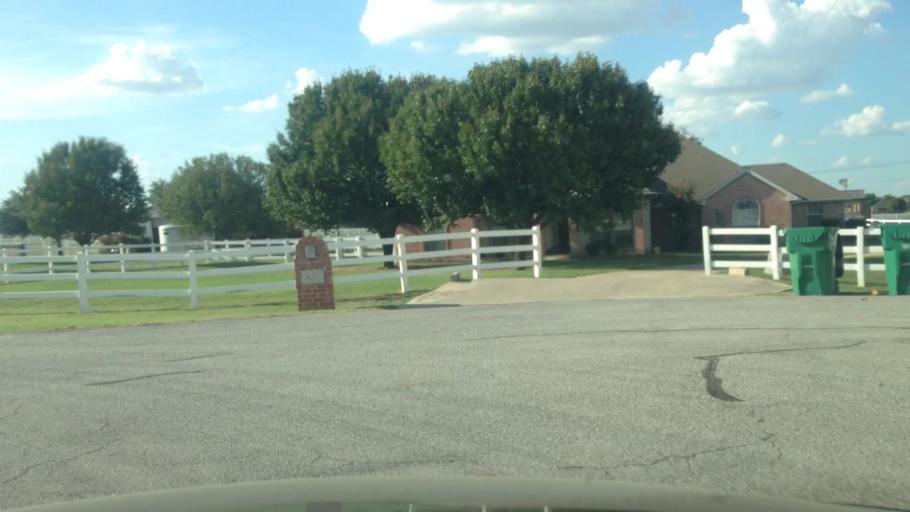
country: US
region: Texas
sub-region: Tarrant County
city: Haslet
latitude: 32.9226
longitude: -97.3769
